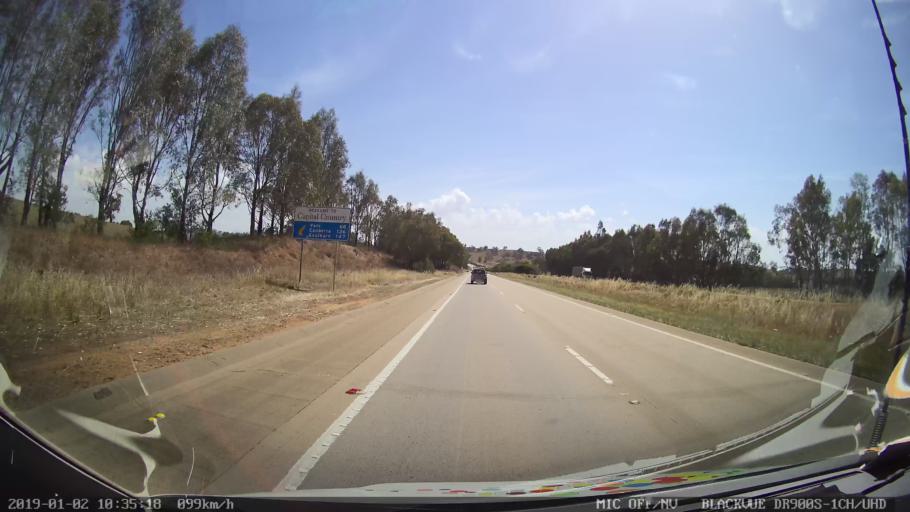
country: AU
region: New South Wales
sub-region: Gundagai
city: Gundagai
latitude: -34.8498
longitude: 148.2927
